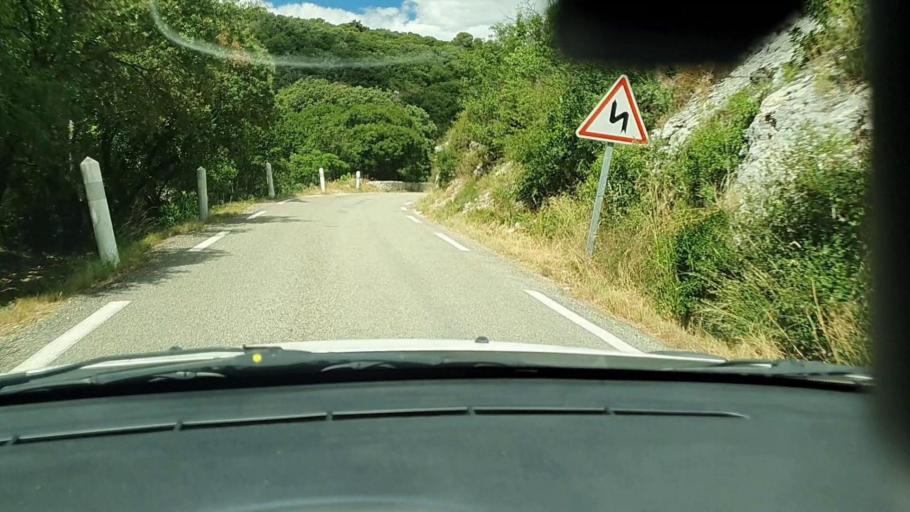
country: FR
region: Languedoc-Roussillon
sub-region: Departement du Gard
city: Cabrieres
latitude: 43.9341
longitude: 4.4740
